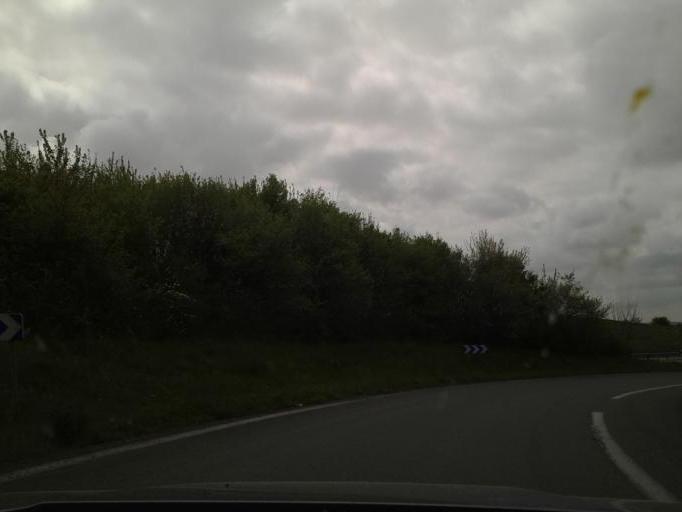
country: FR
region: Pays de la Loire
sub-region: Departement de la Vendee
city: Fontenay-le-Comte
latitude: 46.4340
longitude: -0.8190
